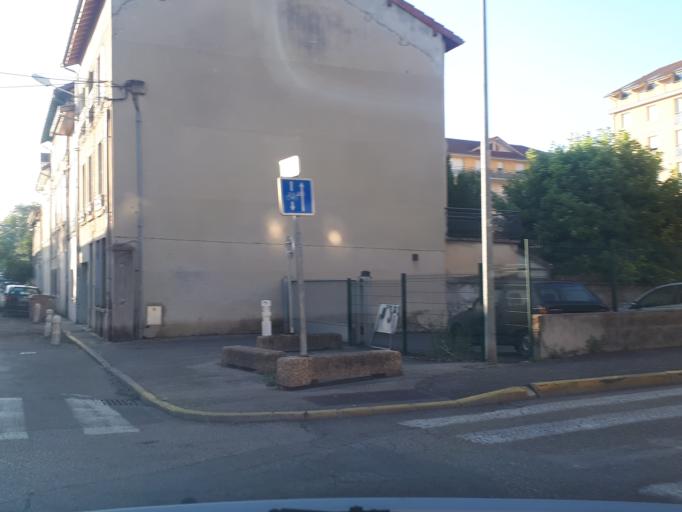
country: FR
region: Rhone-Alpes
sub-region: Departement de l'Isere
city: Bourgoin
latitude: 45.5857
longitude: 5.2811
